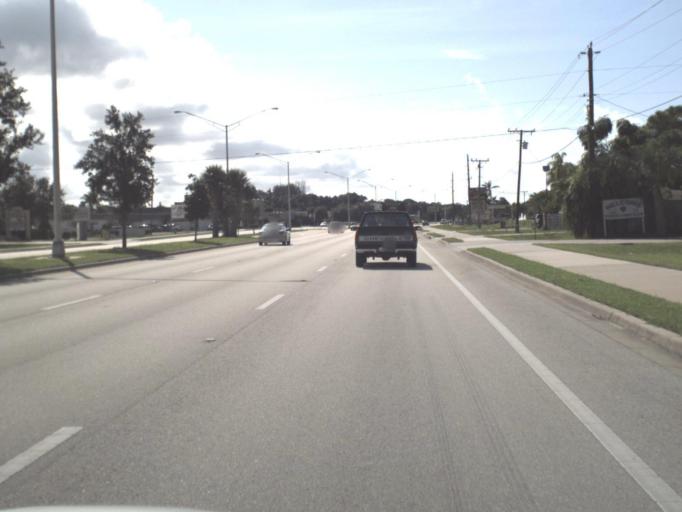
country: US
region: Florida
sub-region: Sarasota County
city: Laurel
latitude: 27.1339
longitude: -82.4554
